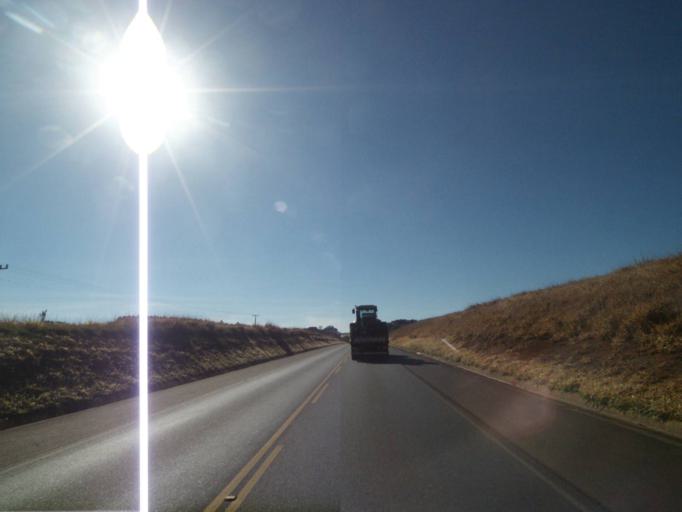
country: BR
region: Parana
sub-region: Tibagi
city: Tibagi
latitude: -24.4638
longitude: -50.4350
